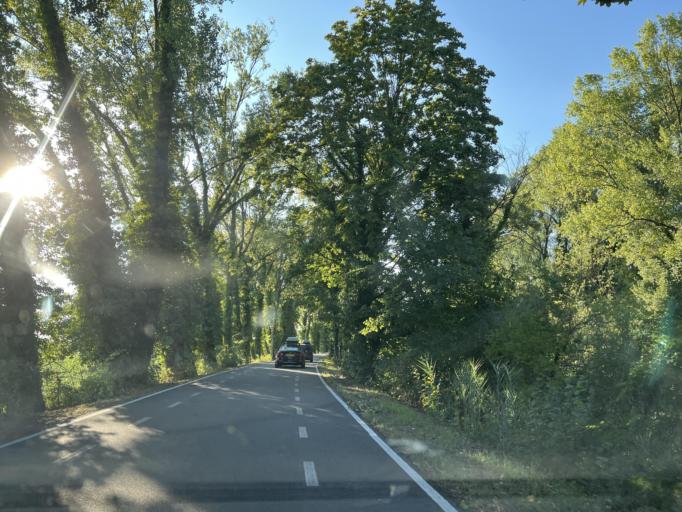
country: IT
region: Friuli Venezia Giulia
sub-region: Provincia di Gorizia
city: San Canzian d'Isonzo
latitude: 45.7748
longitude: 13.4798
